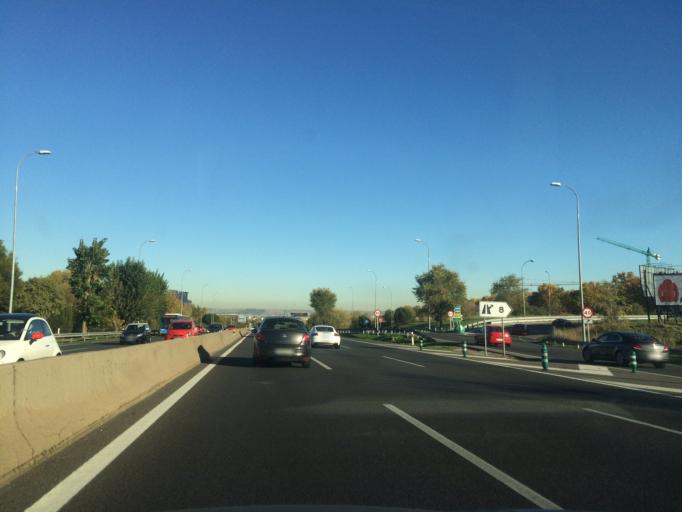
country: ES
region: Madrid
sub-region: Provincia de Madrid
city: San Blas
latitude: 40.4496
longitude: -3.6222
